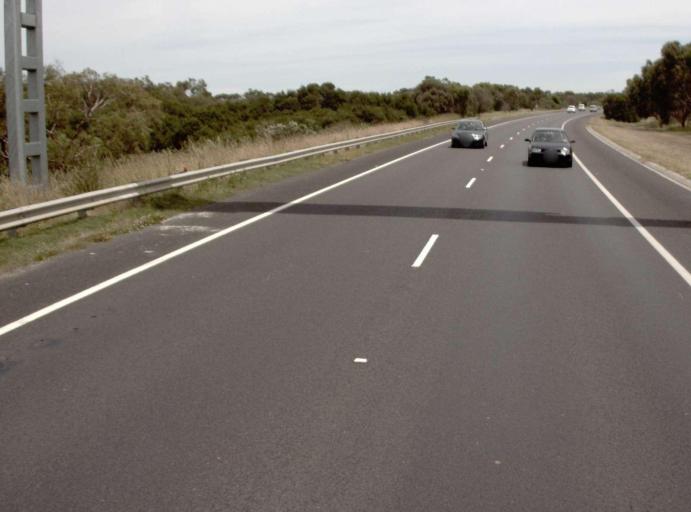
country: AU
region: Victoria
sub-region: Mornington Peninsula
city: Mount Martha
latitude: -38.2847
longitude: 145.0517
